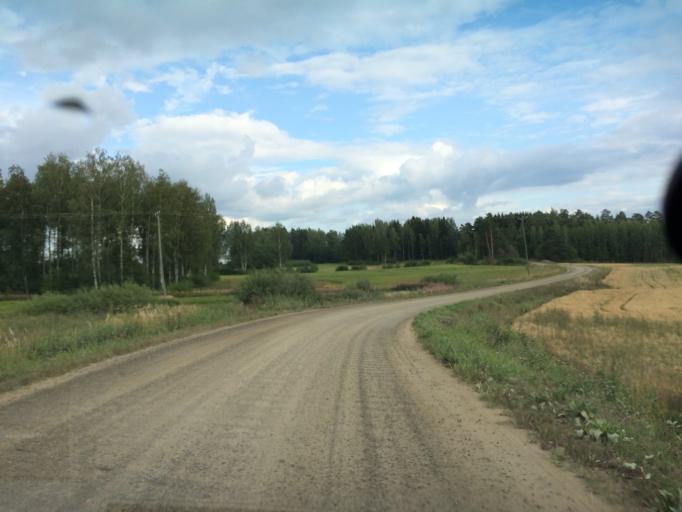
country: FI
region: Pirkanmaa
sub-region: Tampere
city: Luopioinen
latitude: 61.2643
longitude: 24.6996
